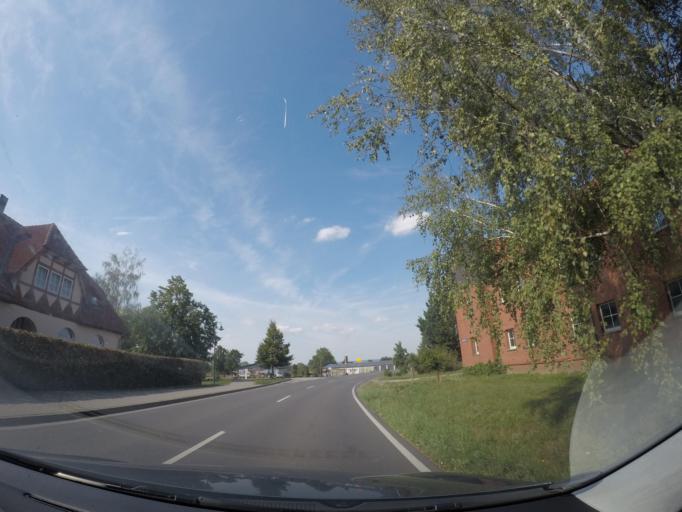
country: DE
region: Saxony-Anhalt
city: Wasserleben
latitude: 51.8935
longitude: 10.7652
